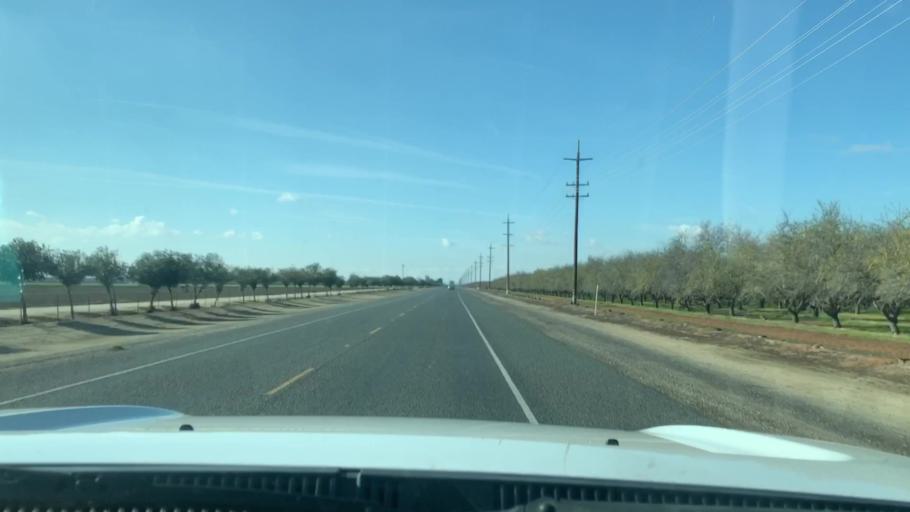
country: US
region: California
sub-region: Kern County
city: Wasco
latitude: 35.6015
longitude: -119.4074
